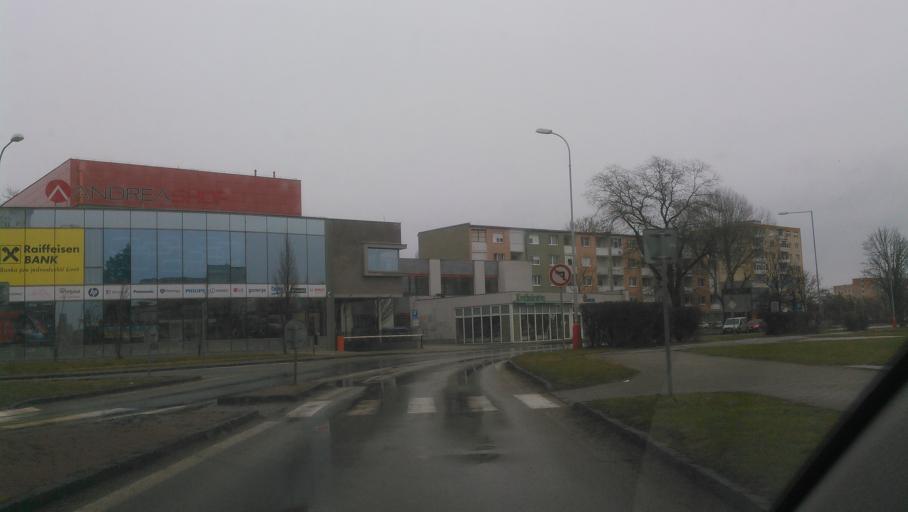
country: SK
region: Nitriansky
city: Sellye
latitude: 48.1486
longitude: 17.8708
